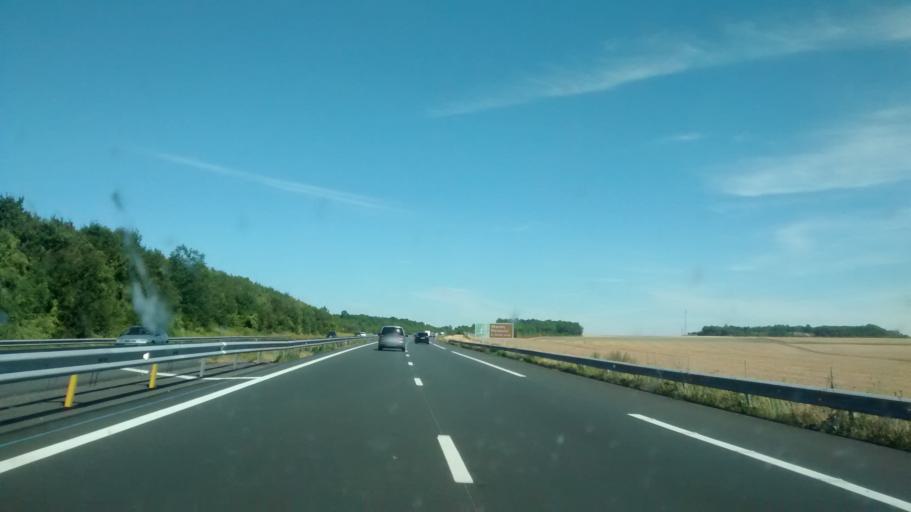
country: FR
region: Poitou-Charentes
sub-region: Departement des Deux-Sevres
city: Beauvoir-sur-Niort
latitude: 46.1733
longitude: -0.5074
